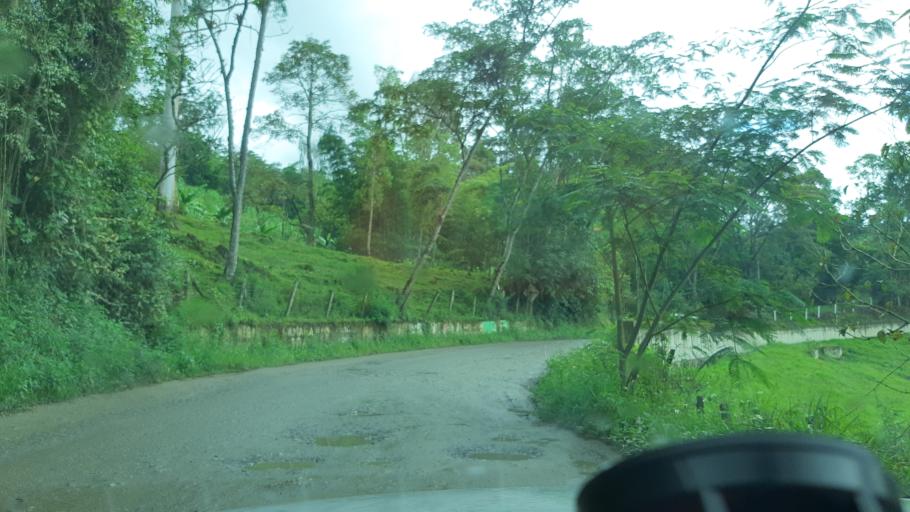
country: CO
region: Boyaca
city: Garagoa
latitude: 5.1168
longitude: -73.3629
